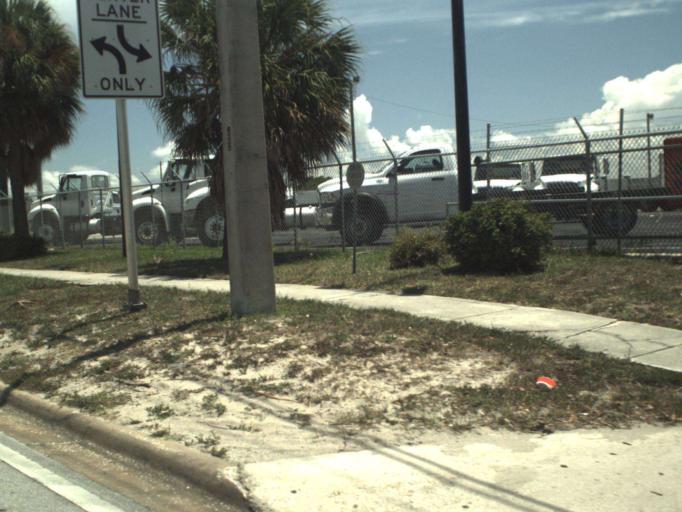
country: US
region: Florida
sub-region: Saint Lucie County
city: Fort Pierce
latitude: 27.4646
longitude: -80.3308
